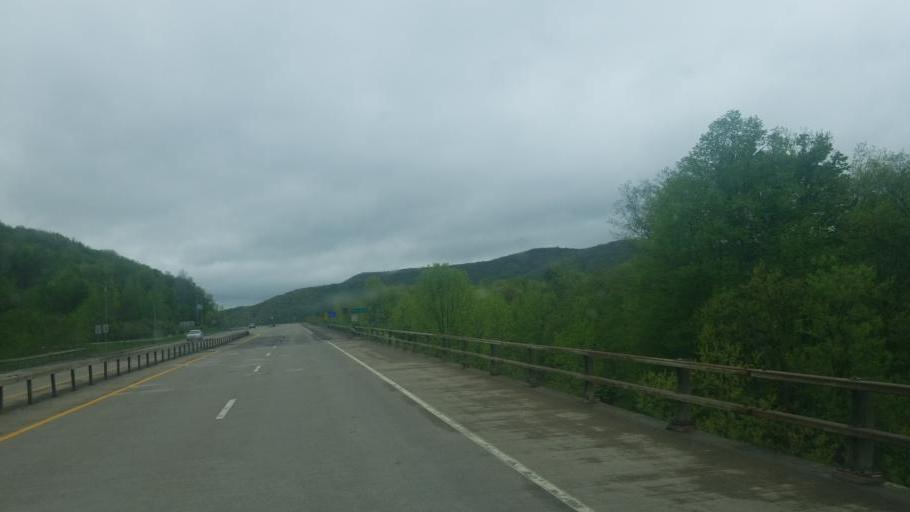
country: US
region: New York
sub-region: Cattaraugus County
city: Salamanca
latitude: 42.0849
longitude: -78.6337
